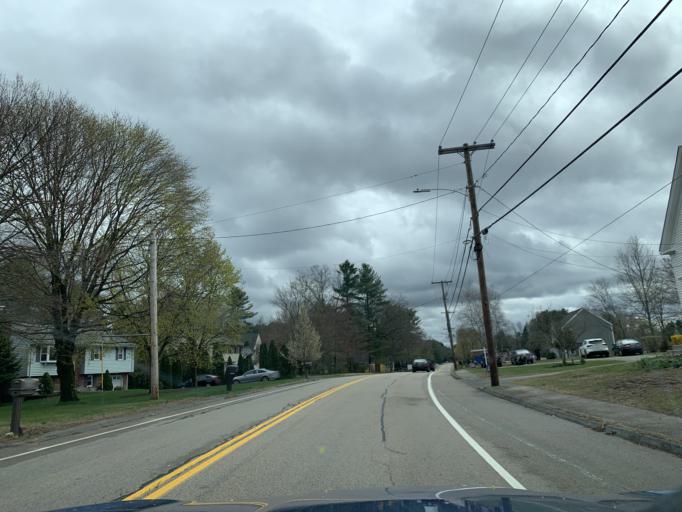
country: US
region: Massachusetts
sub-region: Bristol County
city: Mansfield Center
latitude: 41.9861
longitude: -71.2412
